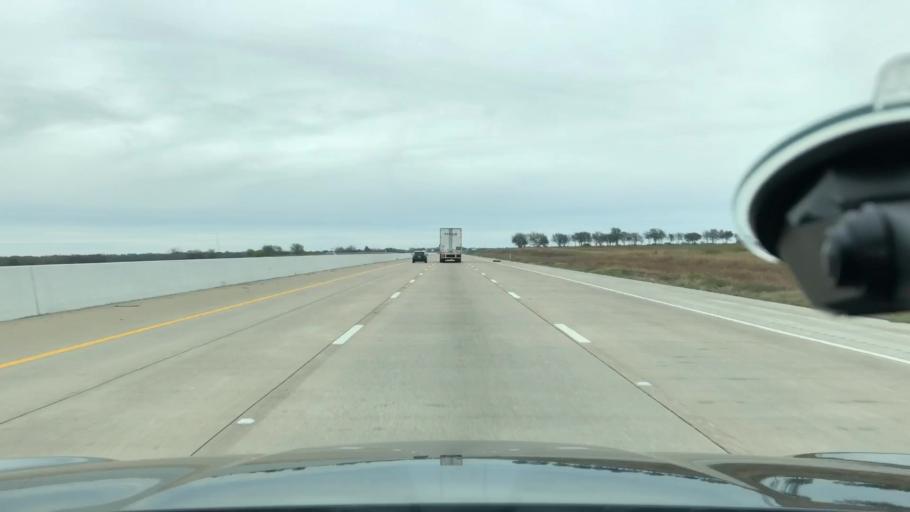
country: US
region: Texas
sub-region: Ellis County
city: Italy
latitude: 32.1623
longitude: -96.9212
